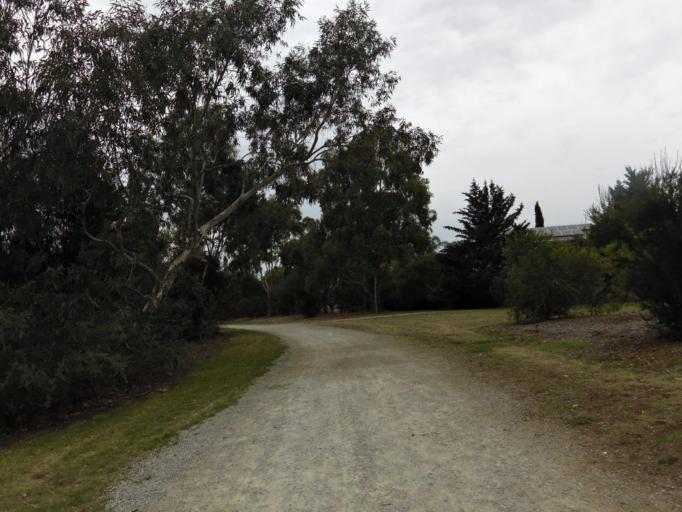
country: AU
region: Victoria
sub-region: Brimbank
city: Taylors Lakes
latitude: -37.7007
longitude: 144.7868
